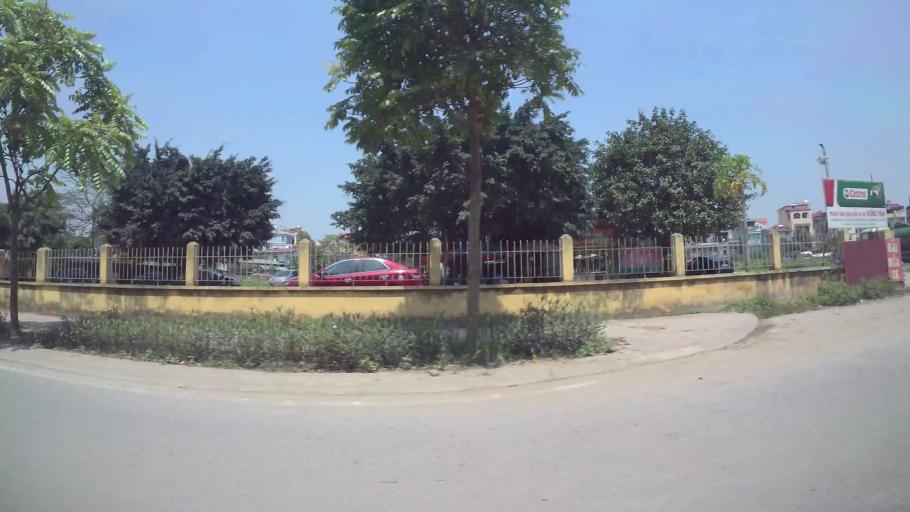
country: VN
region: Ha Noi
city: Hoan Kiem
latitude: 21.0457
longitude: 105.8847
